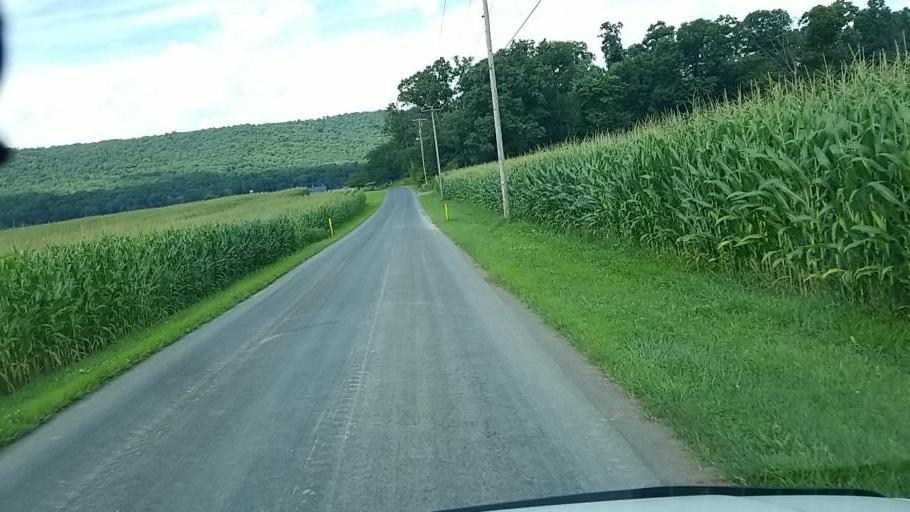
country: US
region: Pennsylvania
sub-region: Dauphin County
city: Elizabethville
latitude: 40.6024
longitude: -76.8515
